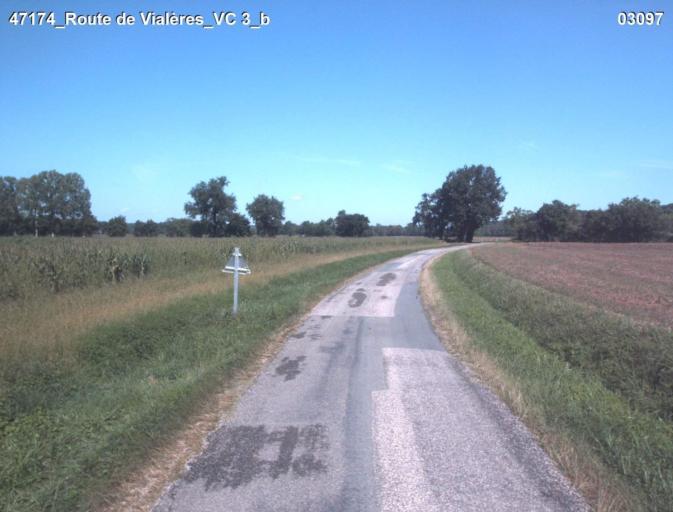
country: FR
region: Aquitaine
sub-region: Departement du Lot-et-Garonne
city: Nerac
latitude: 44.0596
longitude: 0.3854
